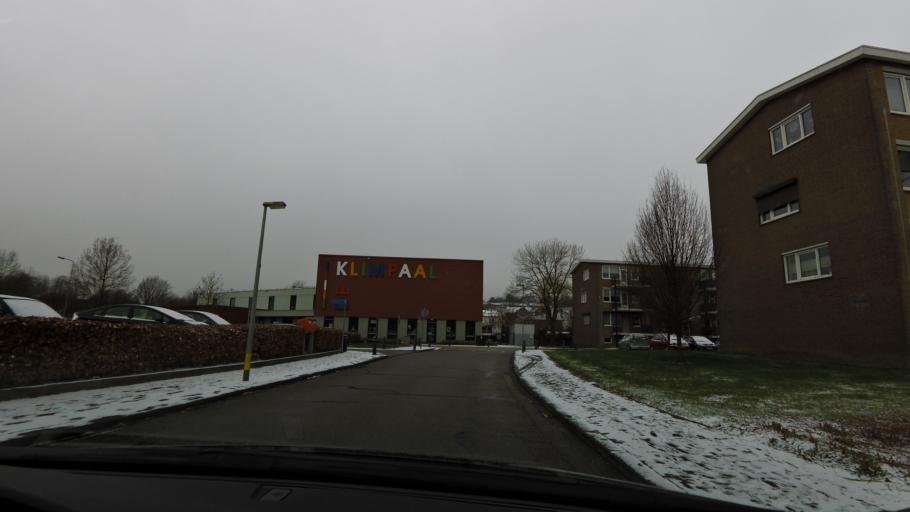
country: NL
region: Limburg
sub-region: Gemeente Simpelveld
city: Simpelveld
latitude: 50.8336
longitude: 5.9762
